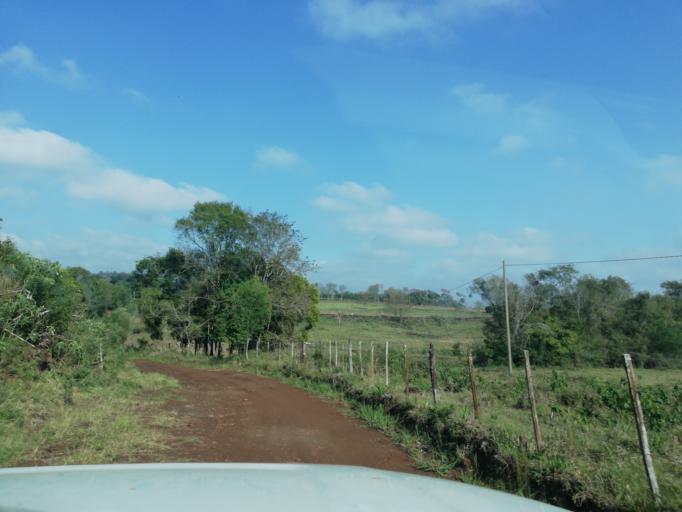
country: AR
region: Misiones
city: Cerro Azul
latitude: -27.5965
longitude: -55.5232
